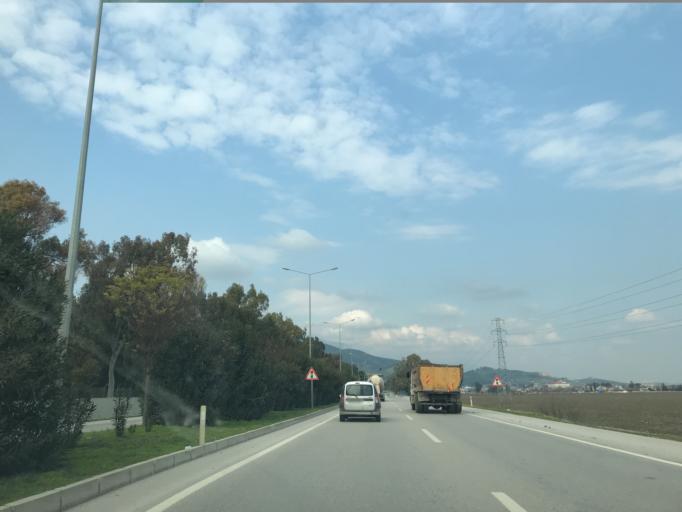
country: TR
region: Hatay
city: Serinyol
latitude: 36.3762
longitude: 36.2274
